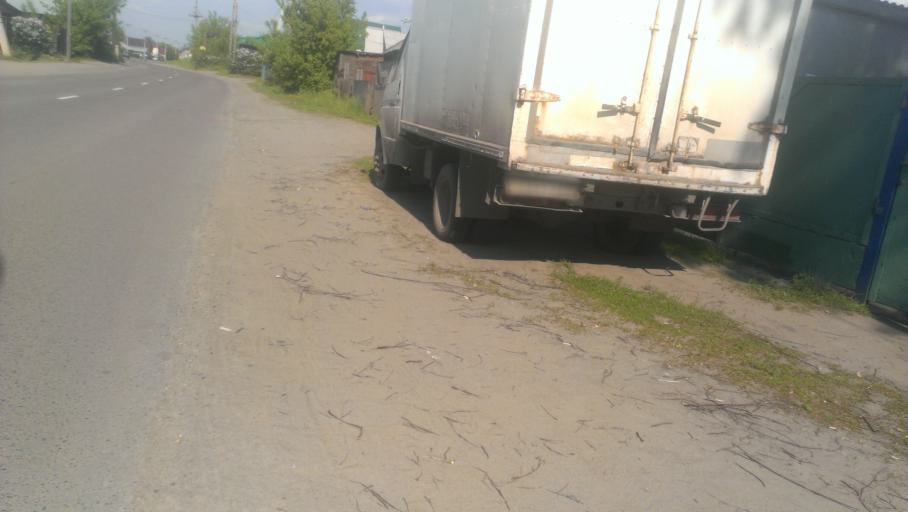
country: RU
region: Altai Krai
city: Novoaltaysk
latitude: 53.3998
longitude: 83.9391
